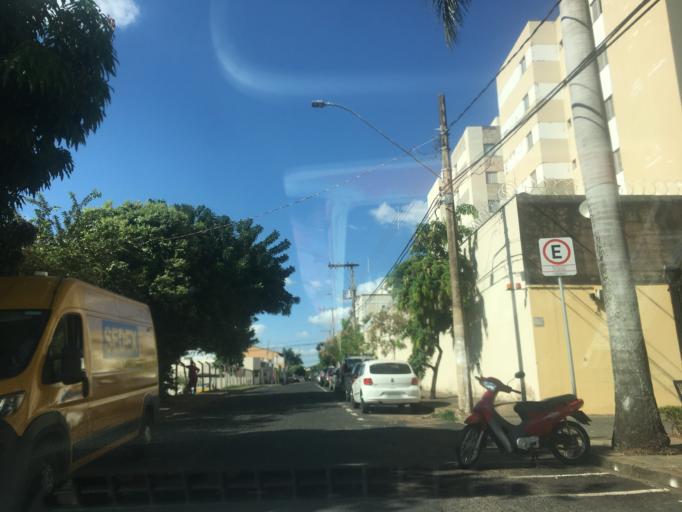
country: BR
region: Minas Gerais
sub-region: Uberlandia
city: Uberlandia
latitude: -18.9054
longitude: -48.2810
